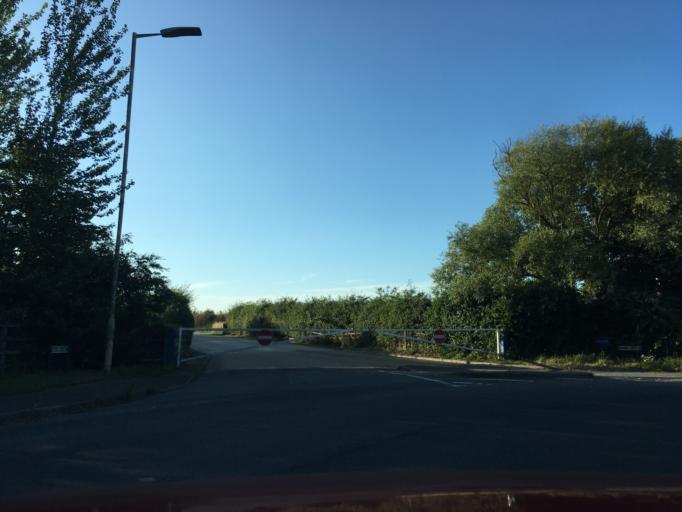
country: GB
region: England
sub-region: Hampshire
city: Tadley
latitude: 51.4044
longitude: -1.1347
